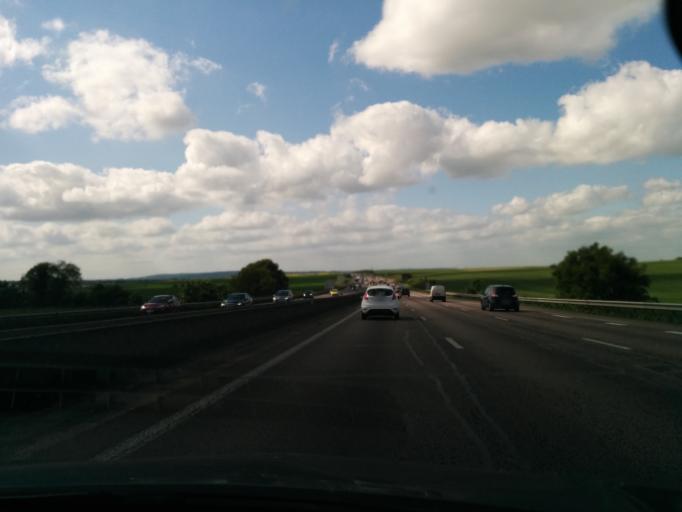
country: FR
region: Ile-de-France
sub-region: Departement des Yvelines
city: Morainvilliers
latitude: 48.9453
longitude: 1.9491
